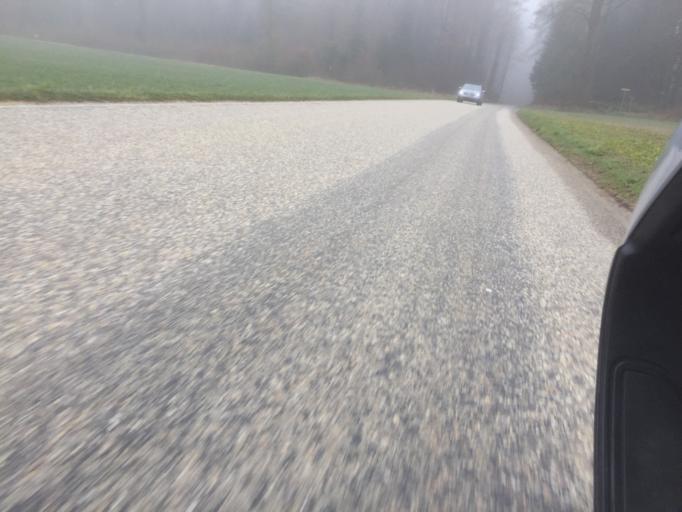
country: CH
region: Bern
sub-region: Seeland District
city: Grossaffoltern
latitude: 47.0967
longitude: 7.3663
